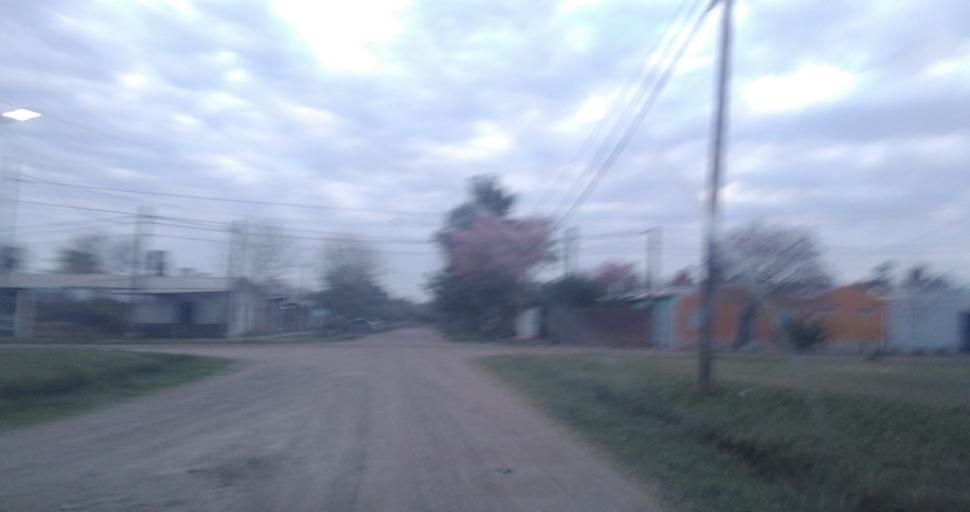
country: AR
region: Chaco
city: Fontana
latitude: -27.4310
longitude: -59.0353
